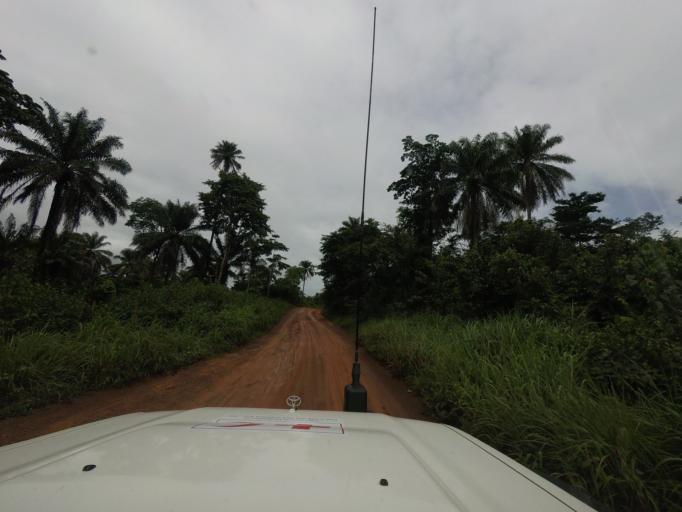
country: GN
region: Nzerekore
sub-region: Nzerekore Prefecture
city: Nzerekore
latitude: 7.7262
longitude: -8.8703
